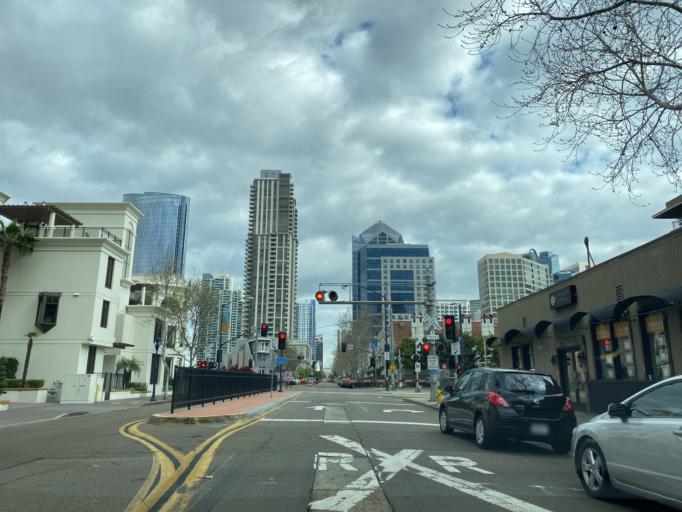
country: US
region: California
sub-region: San Diego County
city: San Diego
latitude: 32.7119
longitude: -117.1692
